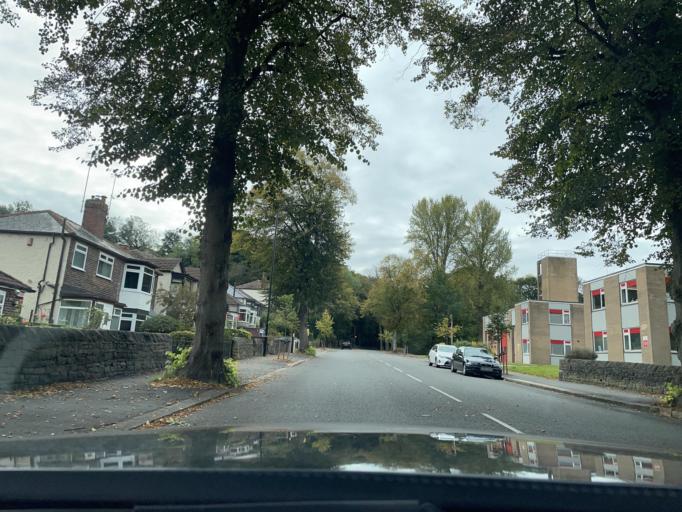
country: GB
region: England
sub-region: Sheffield
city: Oughtibridge
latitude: 53.3986
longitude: -1.5116
